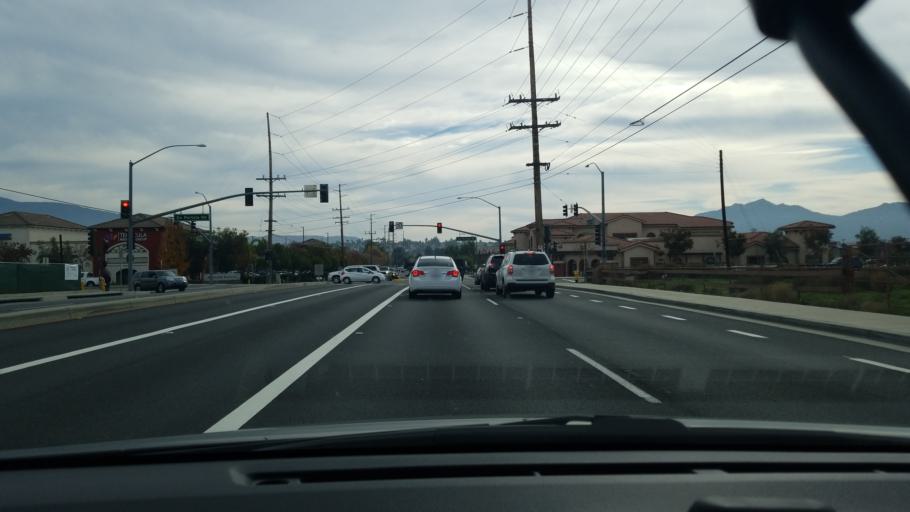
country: US
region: California
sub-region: Riverside County
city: Temecula
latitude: 33.4847
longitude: -117.1032
